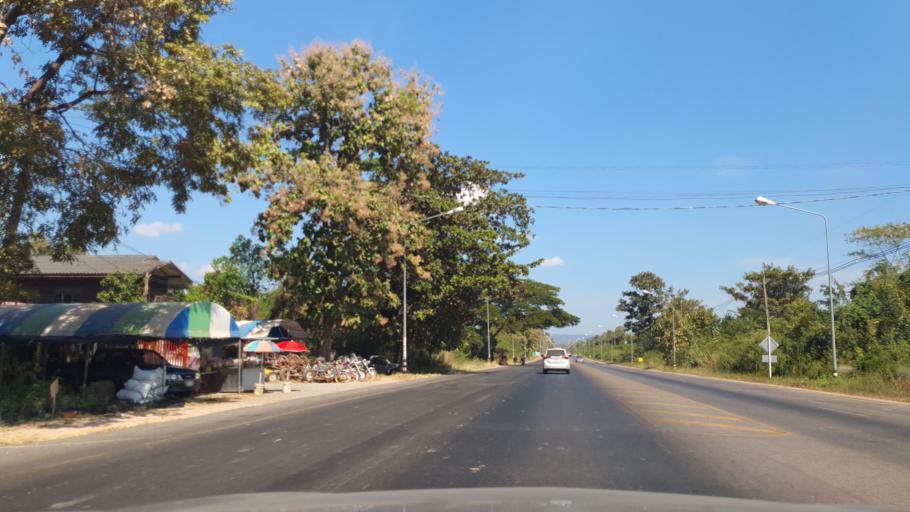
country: TH
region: Kalasin
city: Somdet
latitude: 16.7276
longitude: 103.7621
